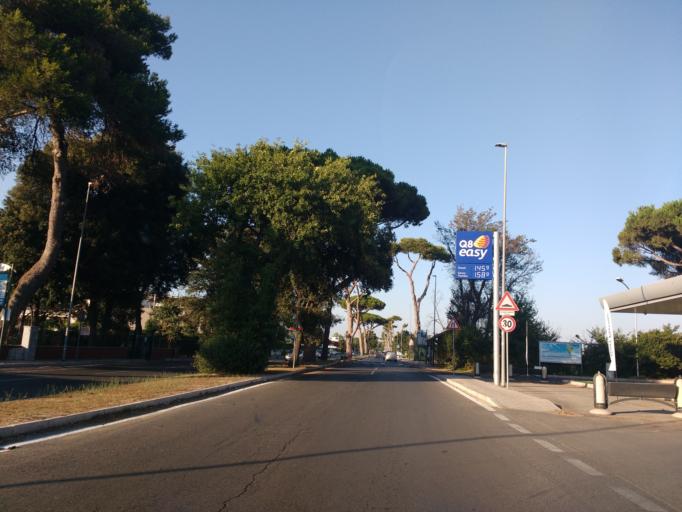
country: IT
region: Latium
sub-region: Citta metropolitana di Roma Capitale
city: Fregene
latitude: 41.8592
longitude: 12.2045
